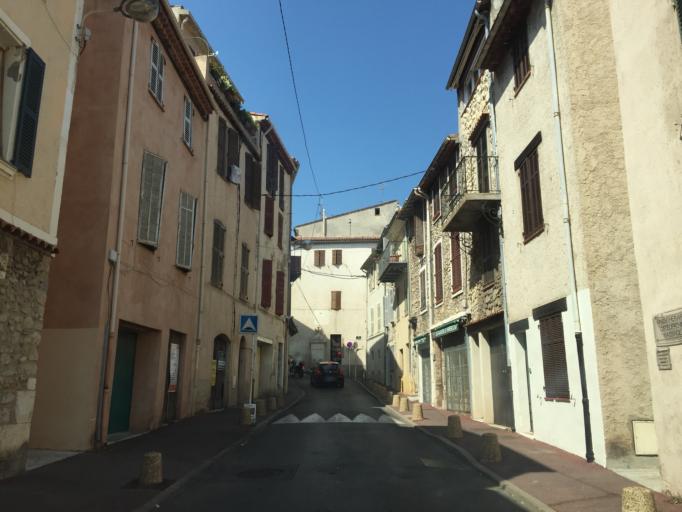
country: FR
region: Provence-Alpes-Cote d'Azur
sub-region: Departement des Alpes-Maritimes
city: Antibes
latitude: 43.5792
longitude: 7.1268
